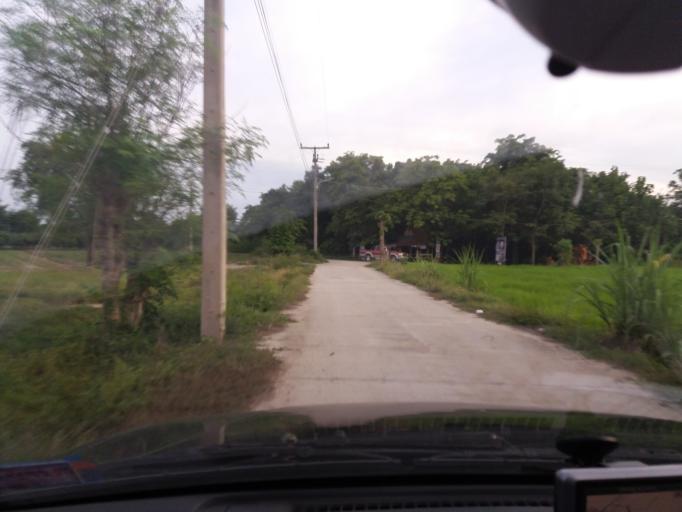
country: TH
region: Suphan Buri
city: Doembang Nangbuat
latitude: 14.8103
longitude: 100.1450
